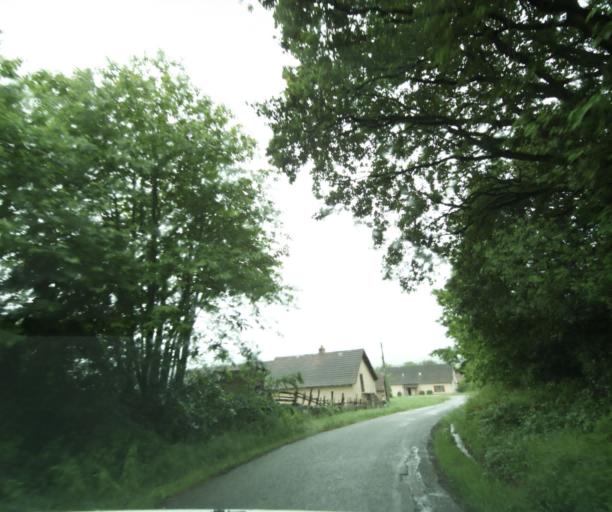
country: FR
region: Bourgogne
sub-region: Departement de Saone-et-Loire
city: Charolles
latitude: 46.3940
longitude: 4.3190
